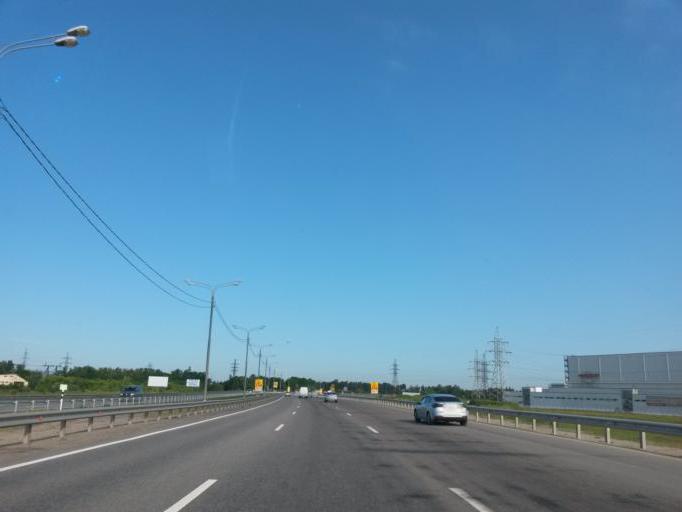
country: RU
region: Moskovskaya
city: Domodedovo
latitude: 55.4607
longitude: 37.7668
